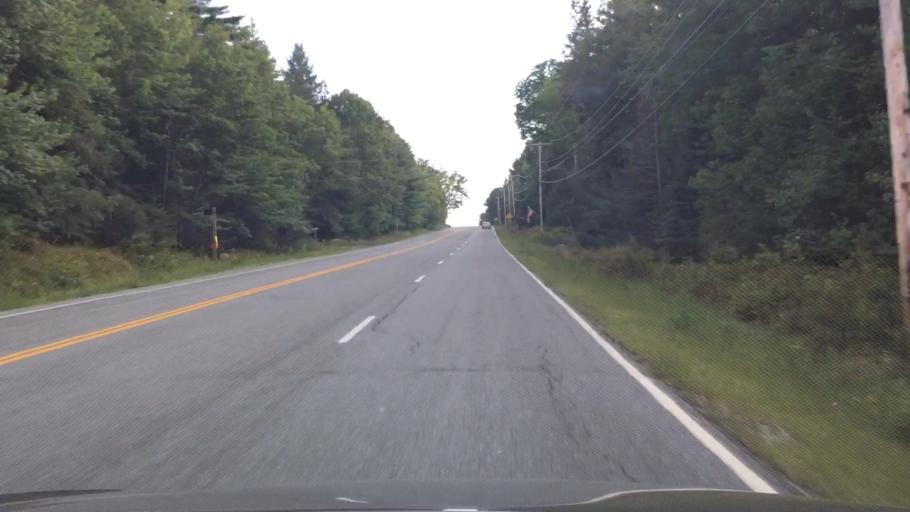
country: US
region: Maine
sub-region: Hancock County
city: Surry
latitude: 44.4921
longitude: -68.5083
